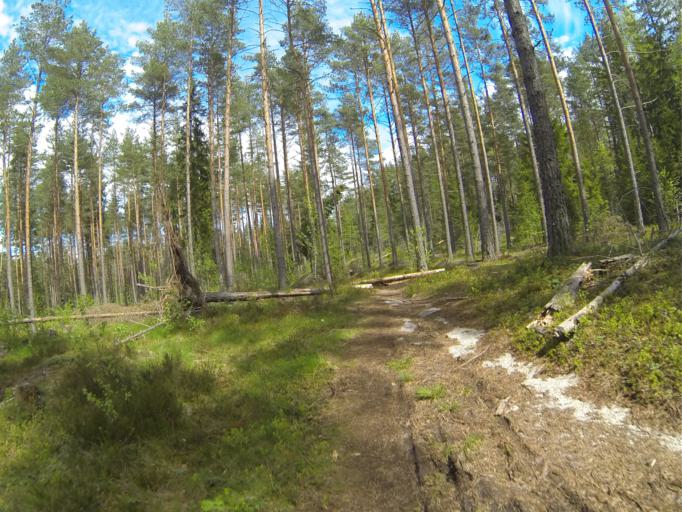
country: FI
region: Varsinais-Suomi
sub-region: Salo
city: Halikko
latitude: 60.3477
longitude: 23.0910
